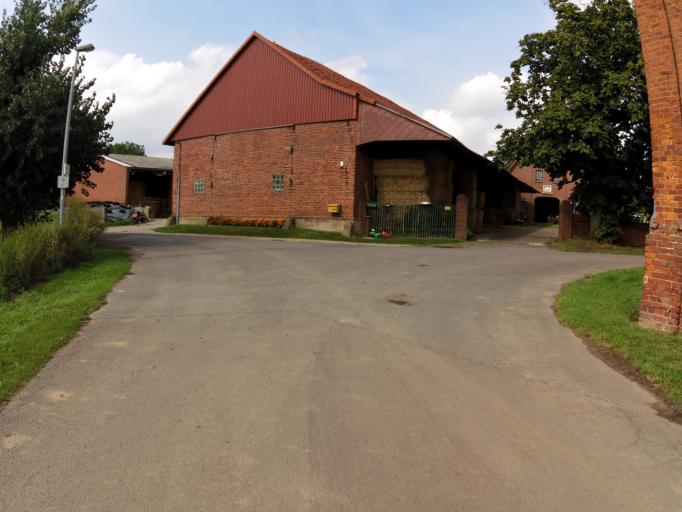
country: DE
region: Lower Saxony
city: Hilgermissen
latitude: 52.8874
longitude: 9.1703
